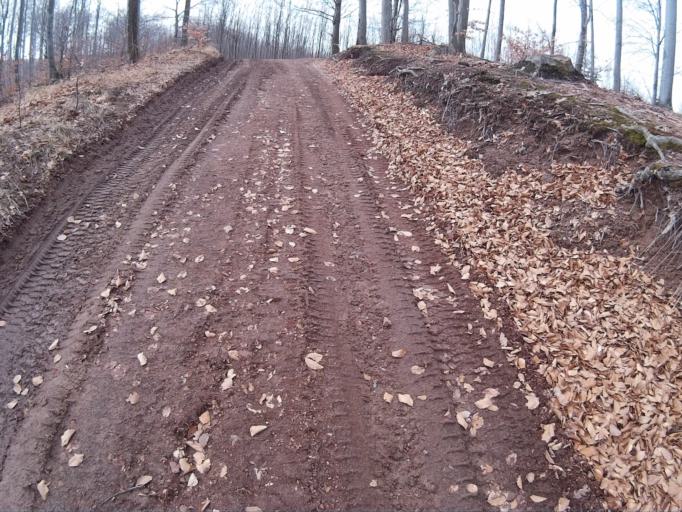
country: HU
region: Borsod-Abauj-Zemplen
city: Tolcsva
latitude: 48.4028
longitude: 21.4198
